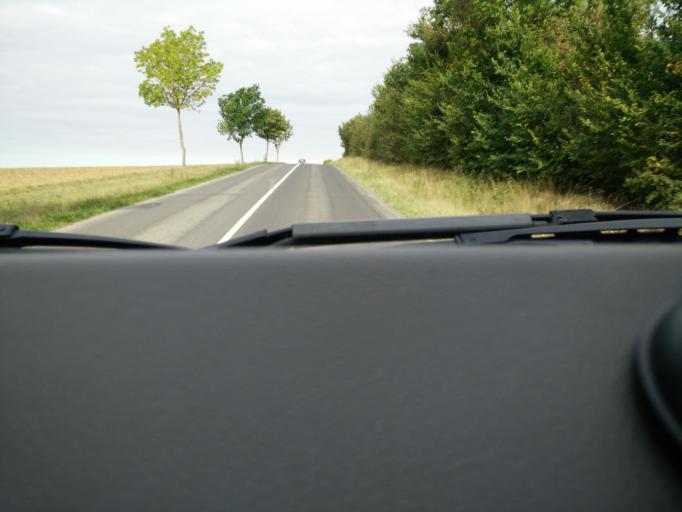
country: FR
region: Lorraine
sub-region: Departement de Meurthe-et-Moselle
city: Montauville
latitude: 48.9056
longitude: 5.9465
